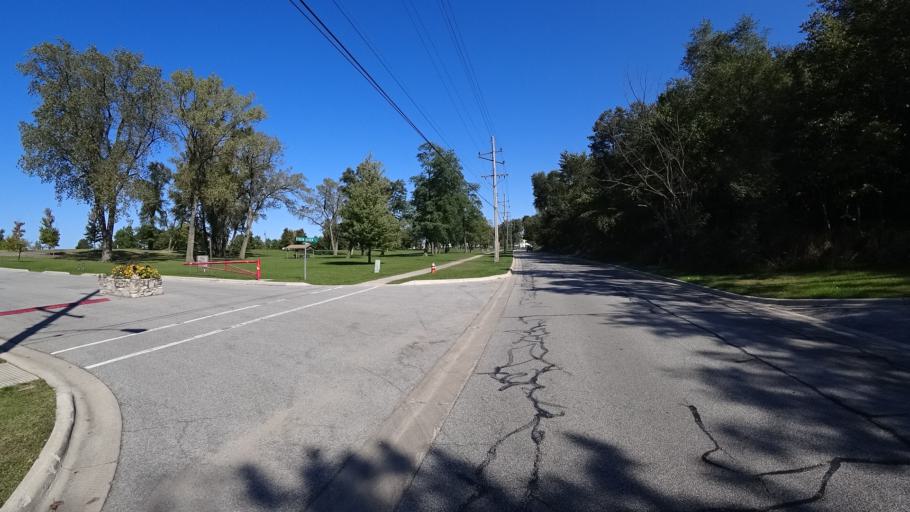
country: US
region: Indiana
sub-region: LaPorte County
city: Michigan City
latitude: 41.7266
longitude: -86.8984
